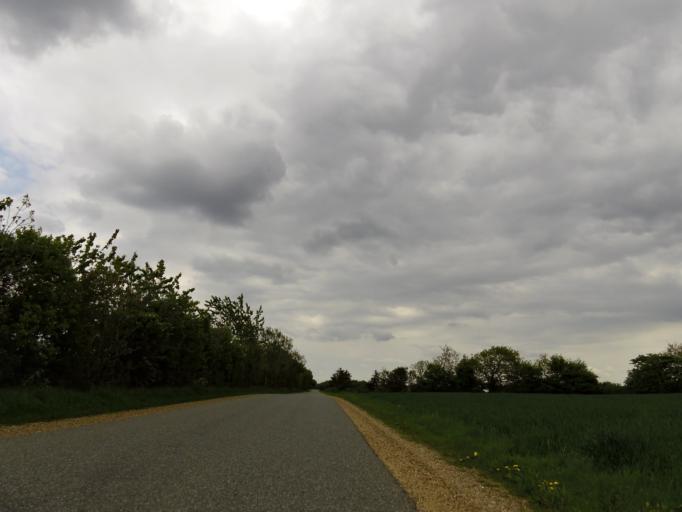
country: DK
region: Central Jutland
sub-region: Holstebro Kommune
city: Vinderup
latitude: 56.5293
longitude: 8.7962
